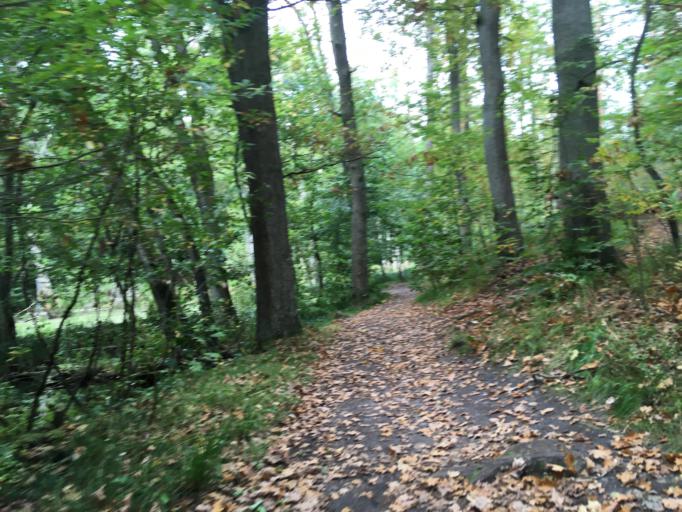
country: DE
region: Brandenburg
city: Birkenwerder
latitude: 52.7057
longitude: 13.3183
